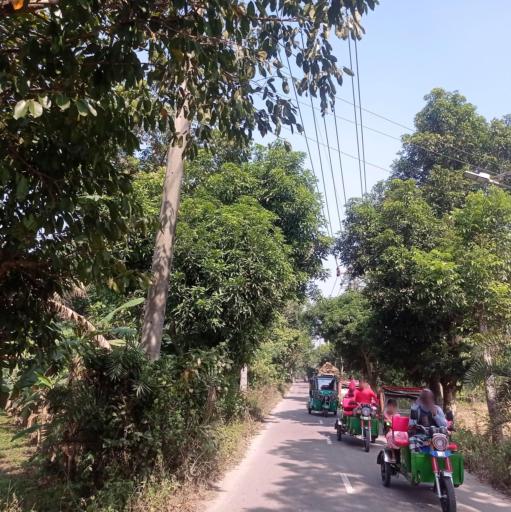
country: BD
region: Dhaka
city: Narsingdi
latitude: 24.0372
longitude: 90.6763
